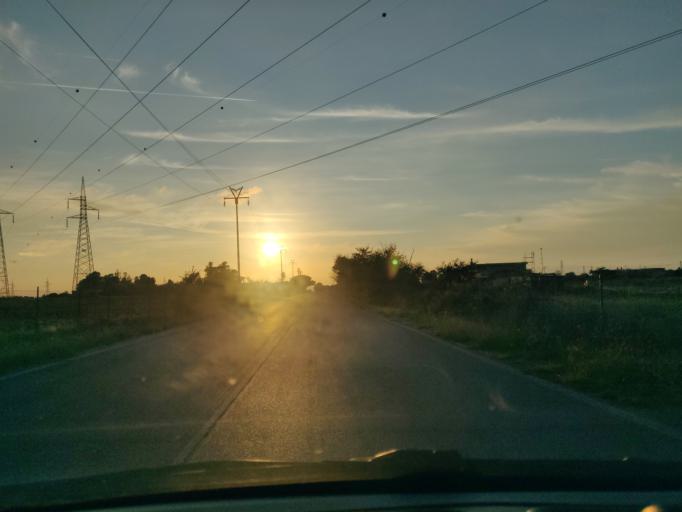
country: IT
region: Latium
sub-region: Citta metropolitana di Roma Capitale
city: Aurelia
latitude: 42.1328
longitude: 11.8092
